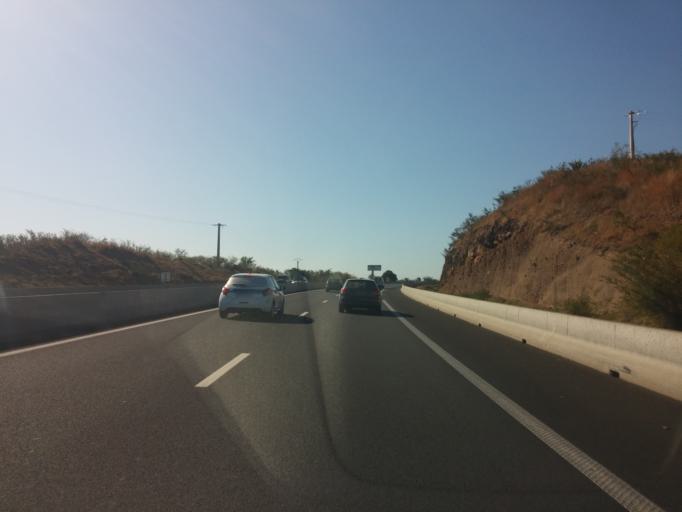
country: RE
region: Reunion
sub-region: Reunion
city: Saint-Paul
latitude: -21.0497
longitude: 55.2483
